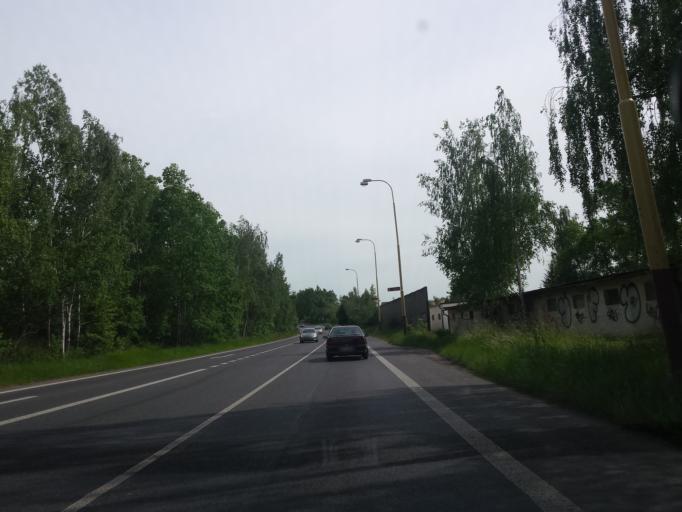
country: CZ
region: Liberecky
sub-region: Okres Ceska Lipa
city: Ceska Lipa
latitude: 50.6749
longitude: 14.5418
